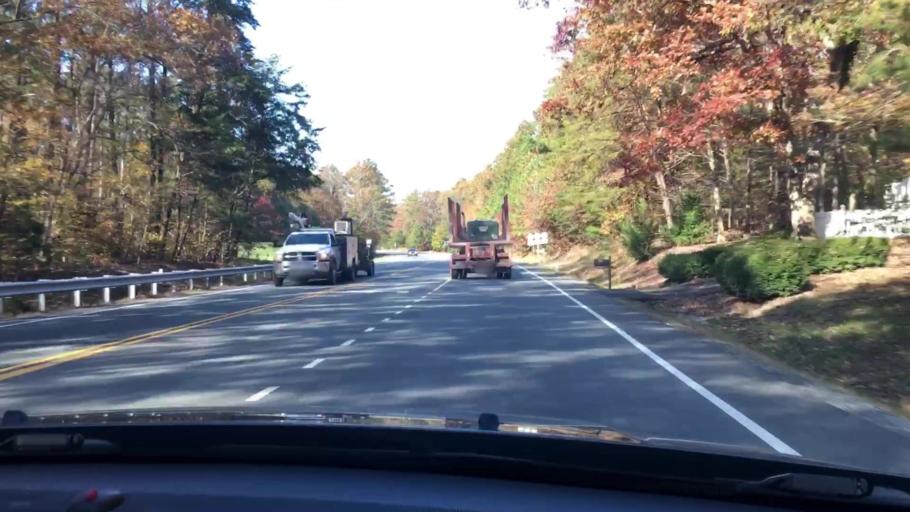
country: US
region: Virginia
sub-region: King William County
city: Central Garage
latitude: 37.7559
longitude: -77.1430
